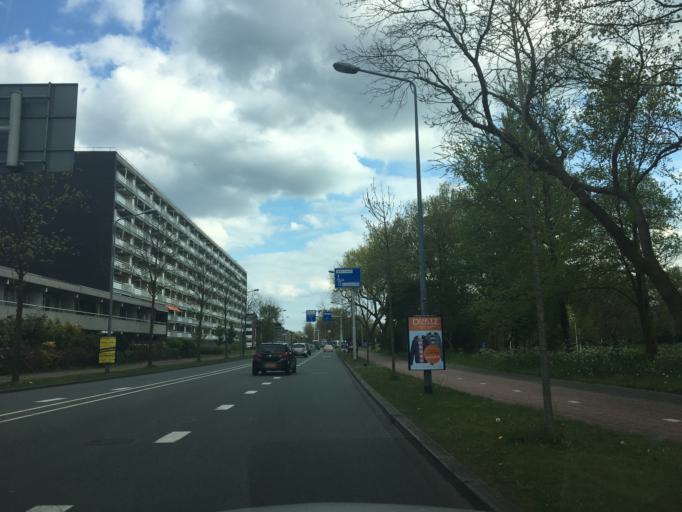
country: NL
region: North Holland
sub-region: Gemeente Wijdemeren
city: Nieuw-Loosdrecht
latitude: 52.2192
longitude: 5.1455
